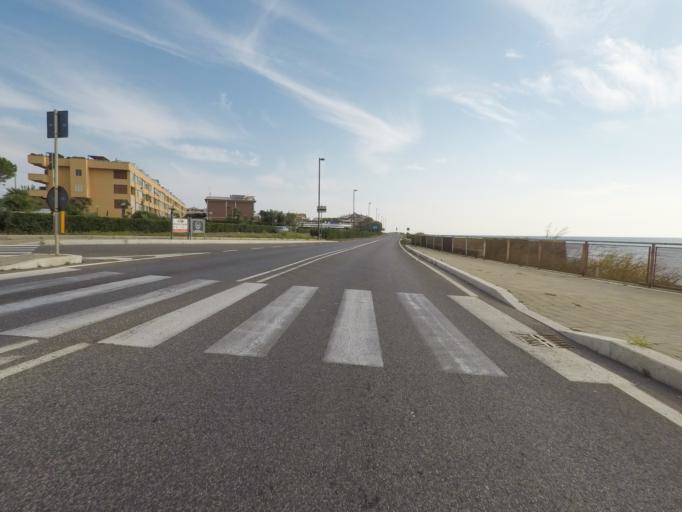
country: IT
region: Latium
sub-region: Citta metropolitana di Roma Capitale
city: Santa Marinella
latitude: 42.0444
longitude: 11.8269
